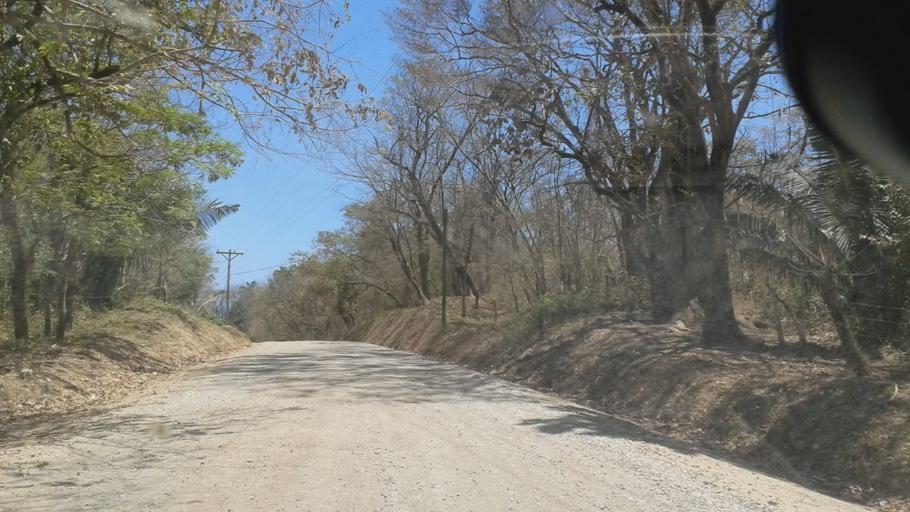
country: CR
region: Guanacaste
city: Samara
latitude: 10.0187
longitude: -85.7214
